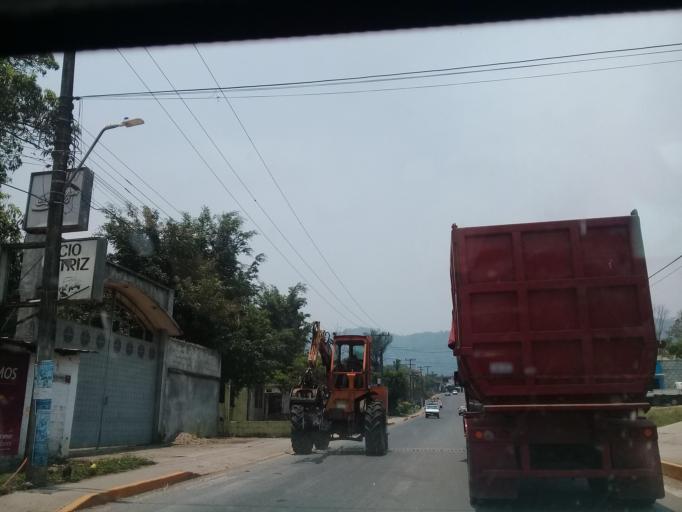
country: MX
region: Veracruz
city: Cosolapa
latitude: 18.5988
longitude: -96.6895
